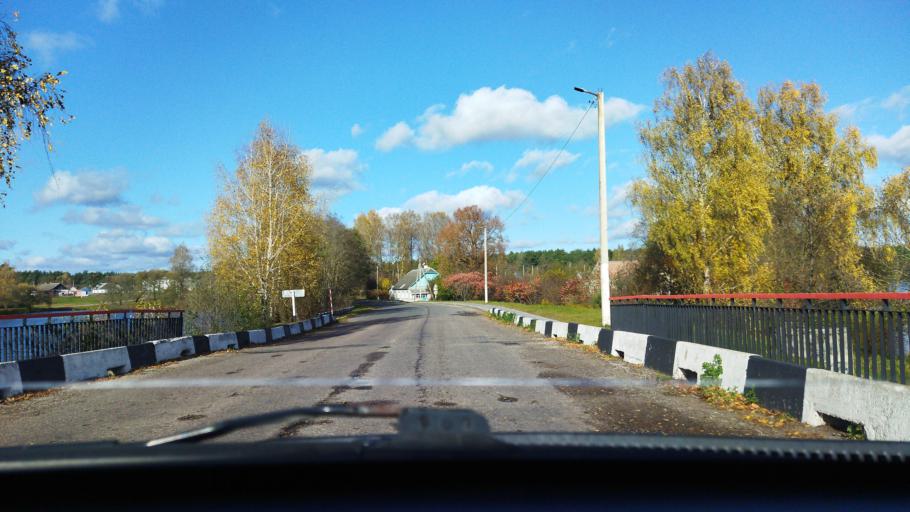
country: BY
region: Minsk
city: Svir
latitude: 54.8056
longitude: 26.2361
